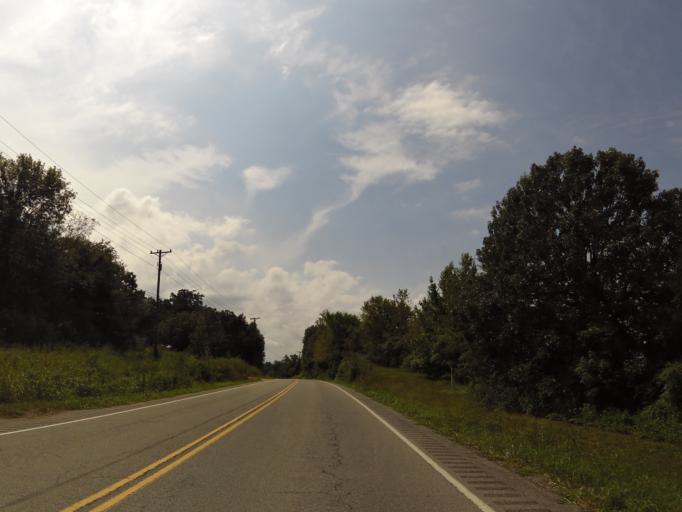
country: US
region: Tennessee
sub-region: Humphreys County
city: New Johnsonville
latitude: 35.8496
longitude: -87.8090
